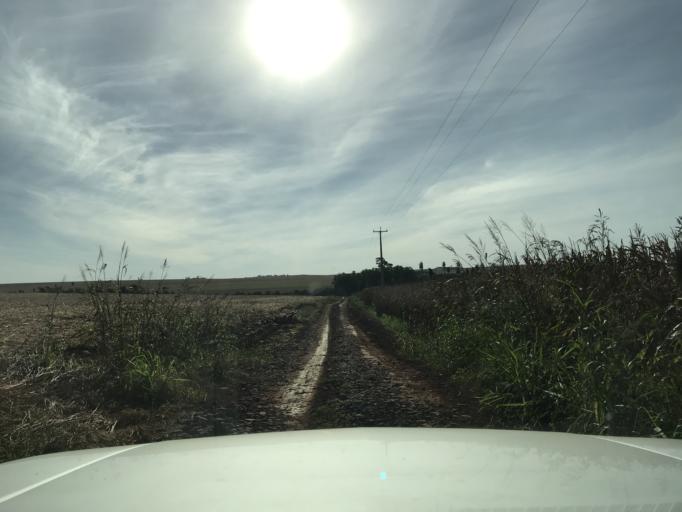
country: BR
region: Parana
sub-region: Palotina
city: Palotina
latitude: -24.2562
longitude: -53.7505
